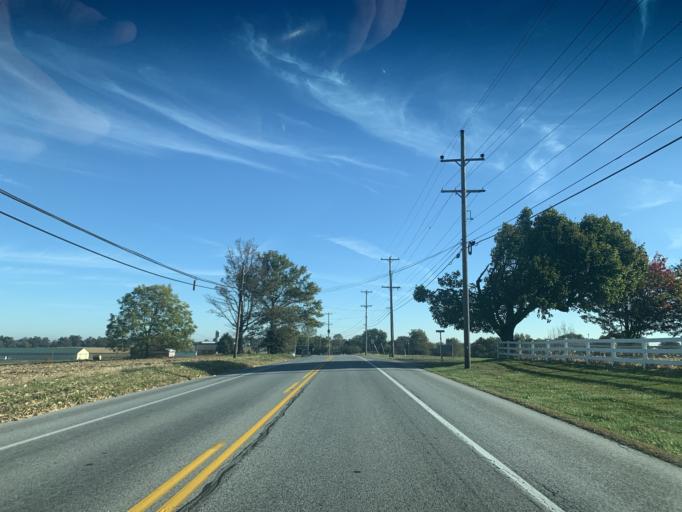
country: US
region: Pennsylvania
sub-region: Chester County
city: Oxford
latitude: 39.8318
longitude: -75.9520
